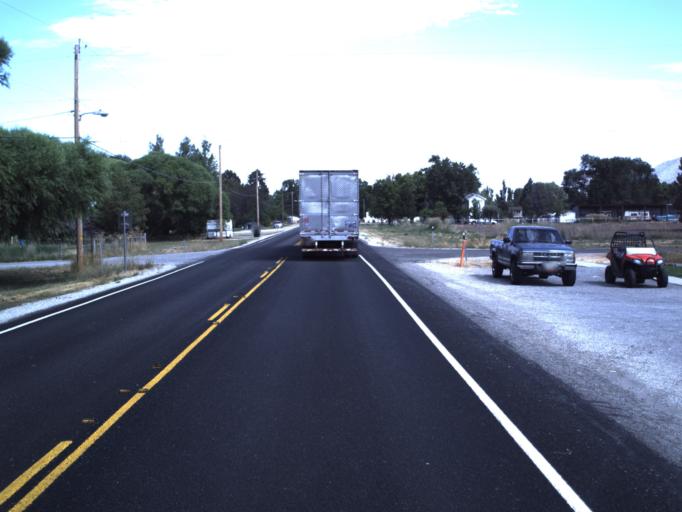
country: US
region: Utah
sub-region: Box Elder County
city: Honeyville
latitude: 41.6078
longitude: -112.1272
